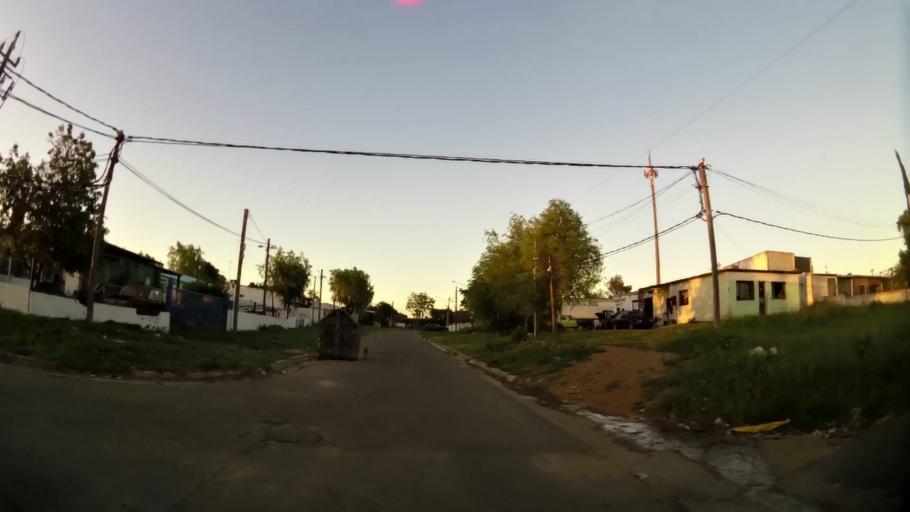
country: UY
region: Montevideo
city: Montevideo
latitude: -34.8291
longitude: -56.1573
